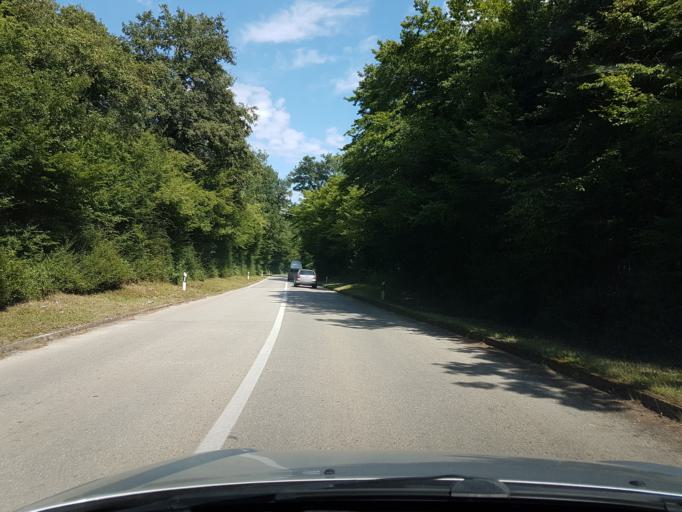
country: HR
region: Istarska
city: Vrsar
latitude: 45.1618
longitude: 13.6726
